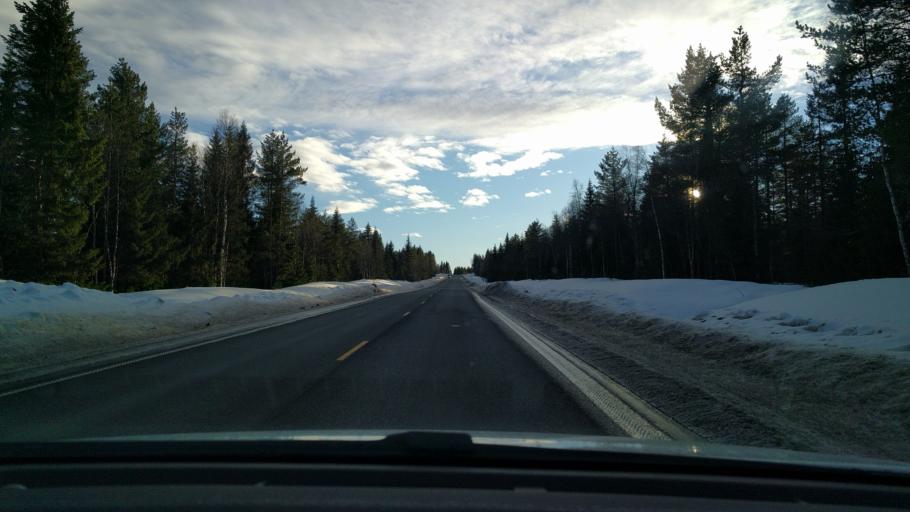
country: NO
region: Hedmark
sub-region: Valer
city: Valer
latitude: 61.0546
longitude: 11.9461
